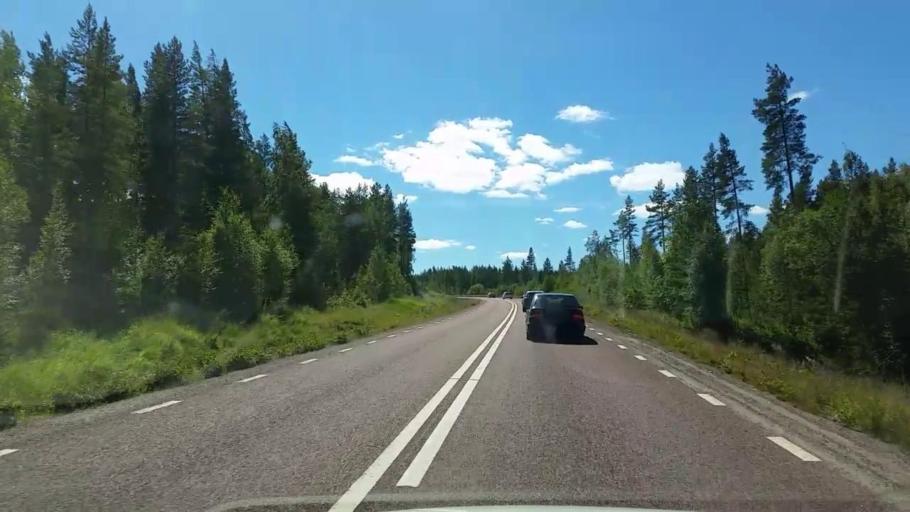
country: SE
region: Gaevleborg
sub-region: Ovanakers Kommun
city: Edsbyn
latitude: 61.2486
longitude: 15.8906
